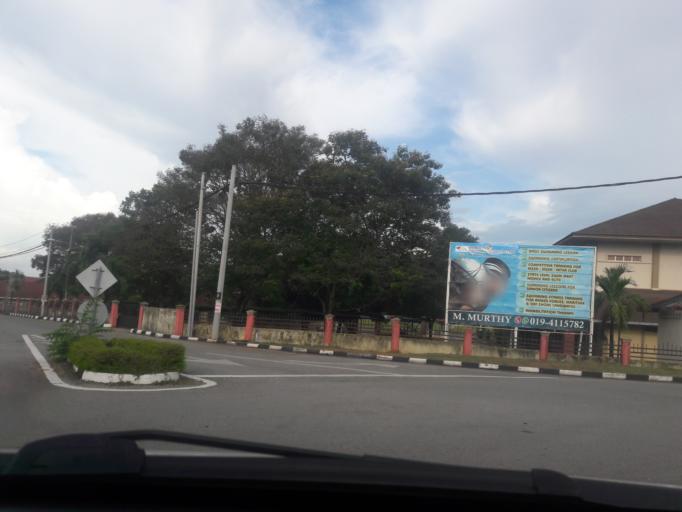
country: MY
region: Kedah
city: Sungai Petani
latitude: 5.6531
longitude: 100.4881
